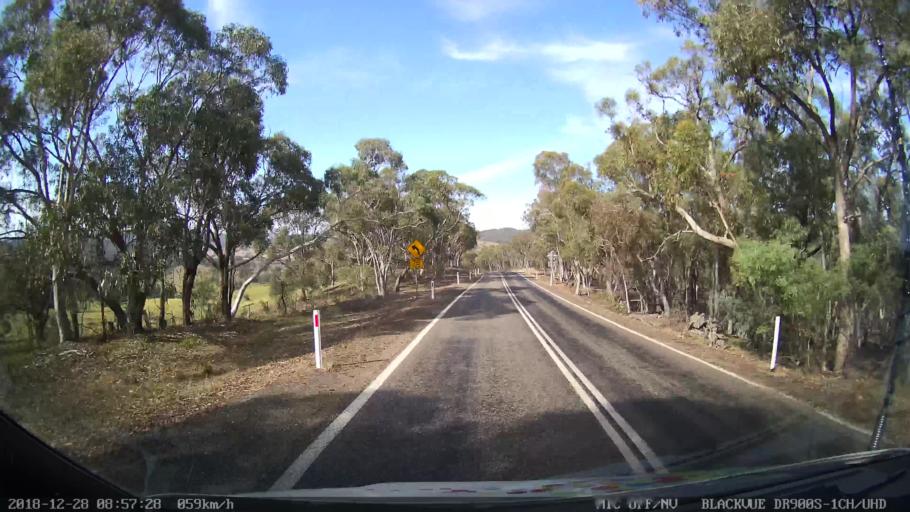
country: AU
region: New South Wales
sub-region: Upper Lachlan Shire
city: Crookwell
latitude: -34.1188
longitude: 149.3352
